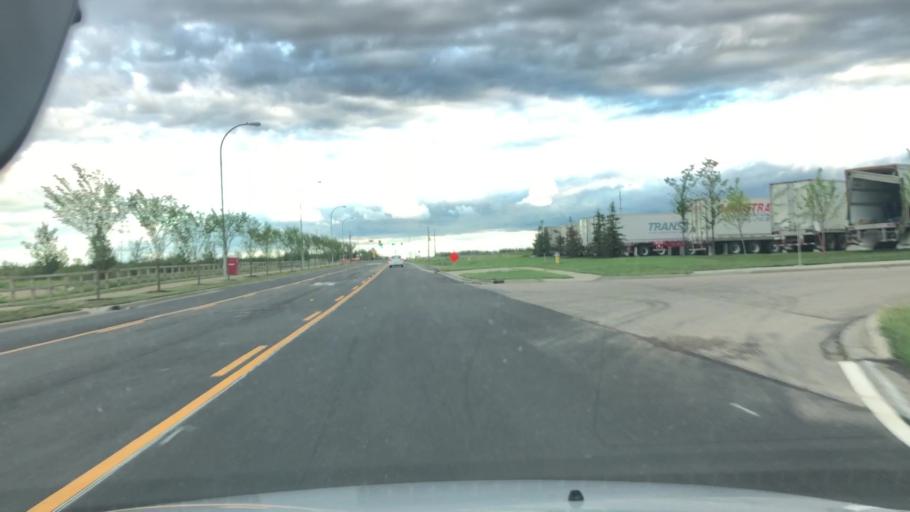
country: CA
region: Alberta
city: St. Albert
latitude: 53.6172
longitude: -113.5698
